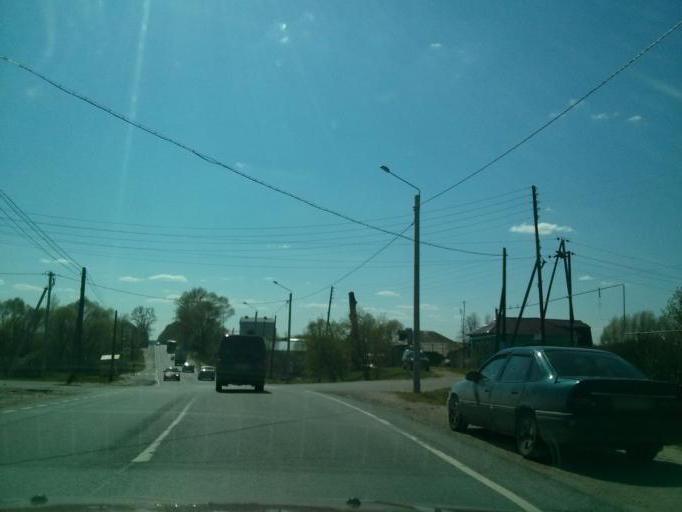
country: RU
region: Nizjnij Novgorod
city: Vorsma
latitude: 56.0376
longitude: 43.3697
